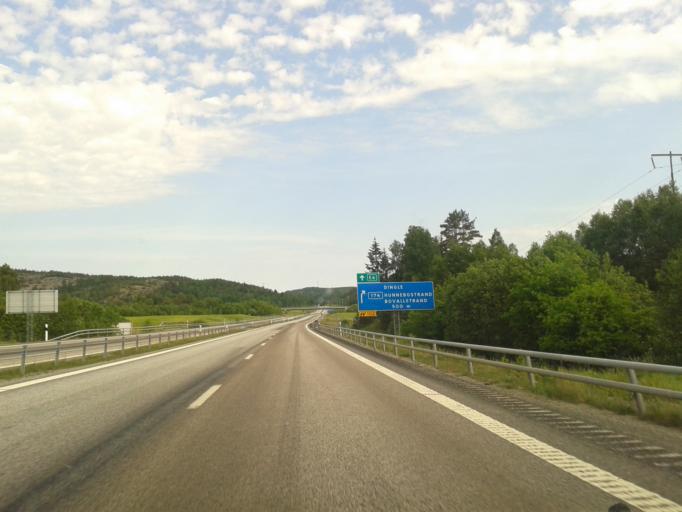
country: SE
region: Vaestra Goetaland
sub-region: Munkedals Kommun
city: Munkedal
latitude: 58.5139
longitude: 11.5536
